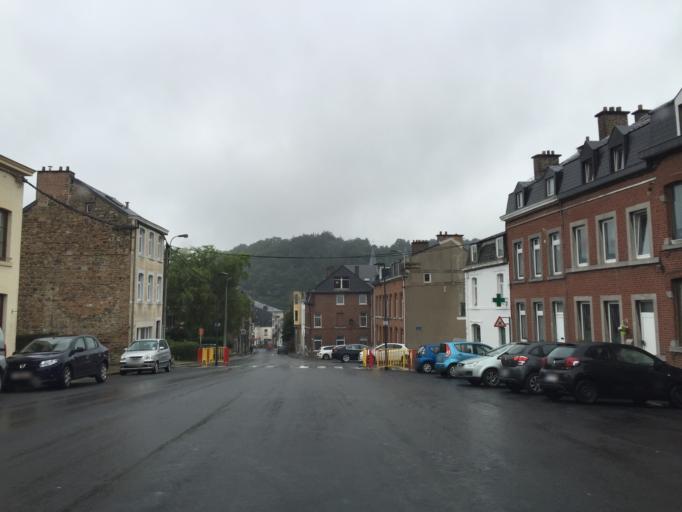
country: BE
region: Wallonia
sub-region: Province de Liege
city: Spa
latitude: 50.4893
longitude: 5.8679
